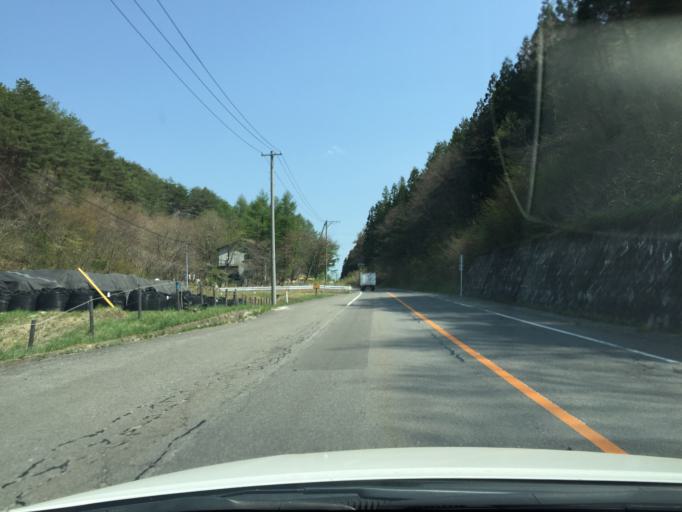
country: JP
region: Fukushima
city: Funehikimachi-funehiki
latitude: 37.4457
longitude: 140.7818
